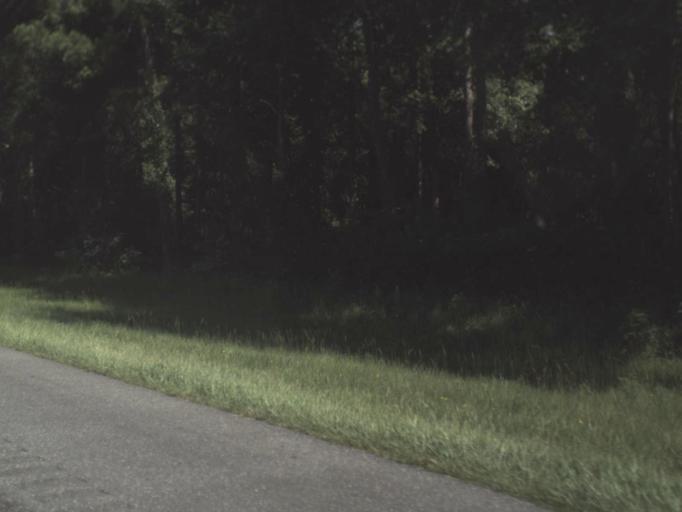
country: US
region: Florida
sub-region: Suwannee County
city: Live Oak
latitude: 30.3443
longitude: -83.1350
